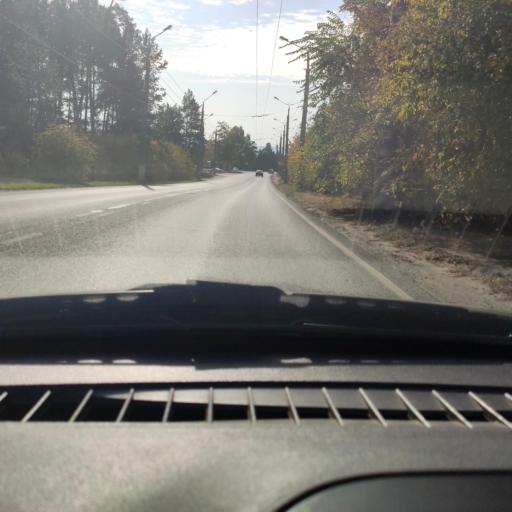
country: RU
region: Samara
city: Tol'yatti
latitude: 53.4781
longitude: 49.3476
